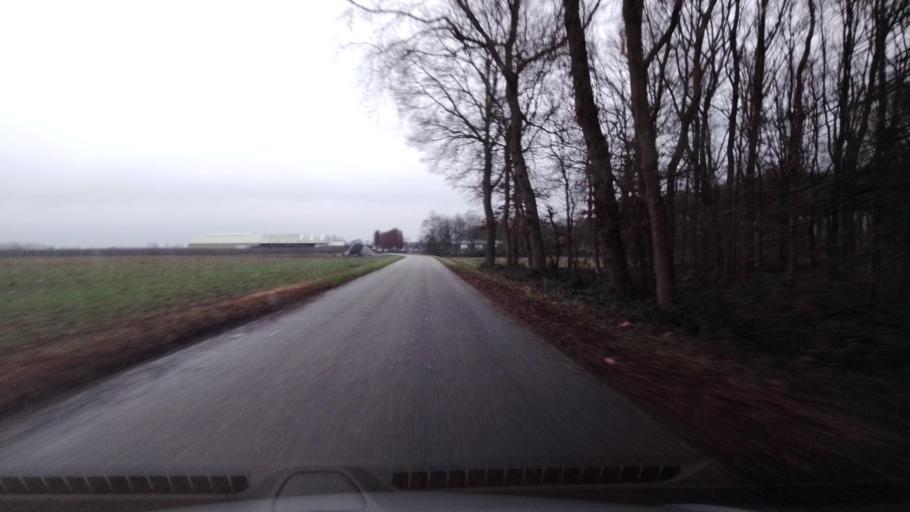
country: NL
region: Limburg
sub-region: Gemeente Bergen
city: Wellerlooi
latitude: 51.5380
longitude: 6.0981
